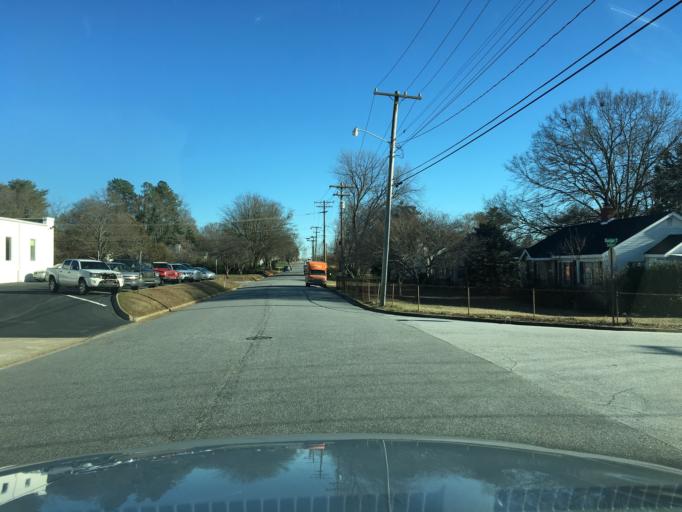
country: US
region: South Carolina
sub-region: Greenville County
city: Greer
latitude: 34.9407
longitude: -82.2394
